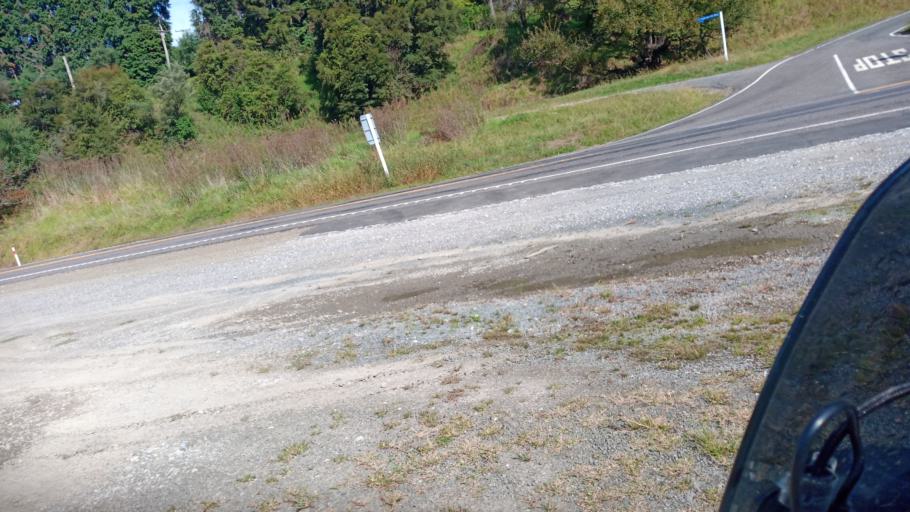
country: NZ
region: Gisborne
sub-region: Gisborne District
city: Gisborne
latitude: -38.4617
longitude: 177.6479
